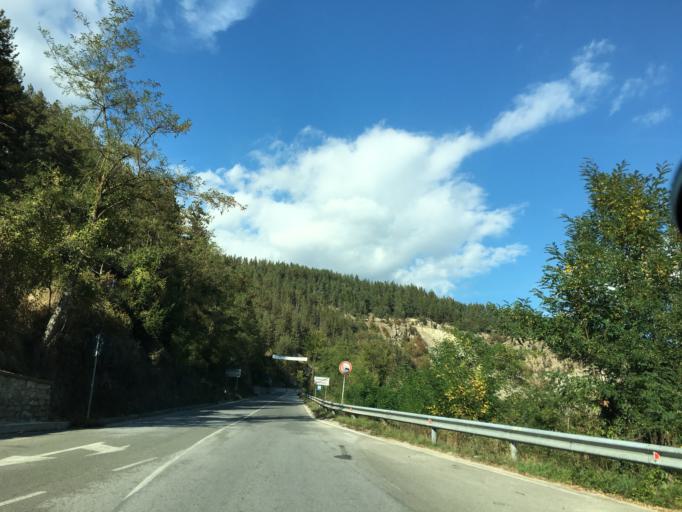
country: BG
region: Smolyan
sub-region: Obshtina Madan
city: Madan
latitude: 41.5323
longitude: 24.9117
